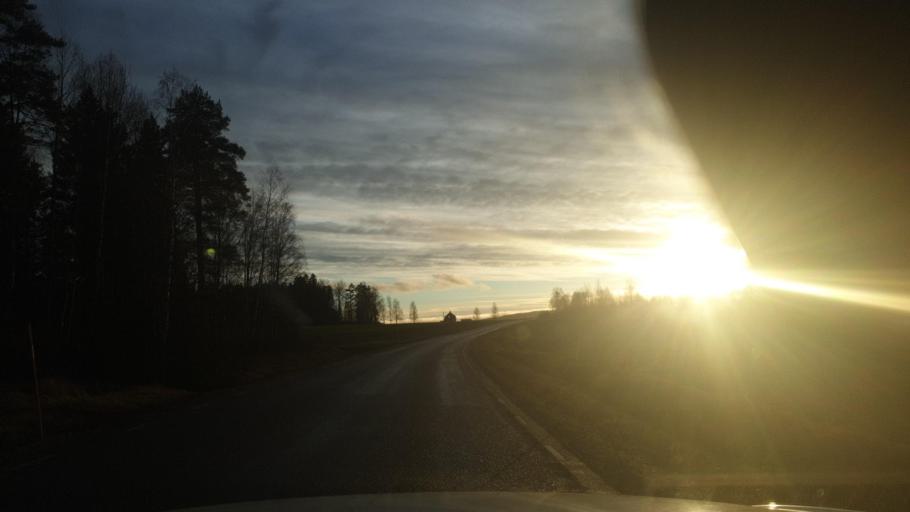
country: SE
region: Vaermland
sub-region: Eda Kommun
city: Charlottenberg
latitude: 59.7627
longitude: 12.1609
